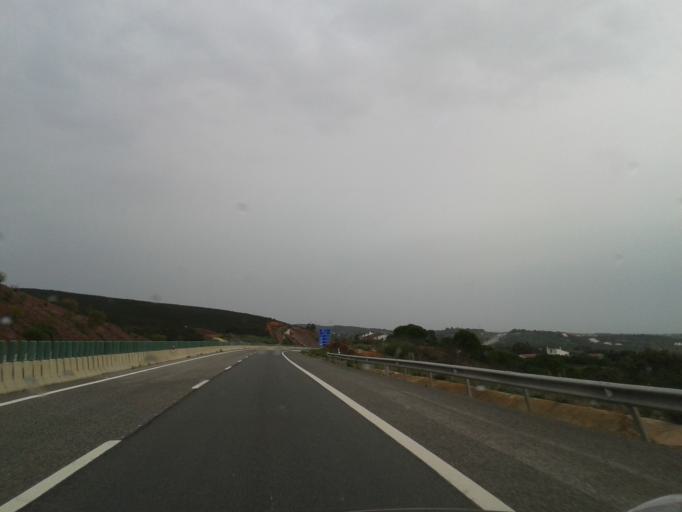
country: PT
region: Faro
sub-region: Lagos
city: Lagos
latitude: 37.1678
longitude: -8.6667
